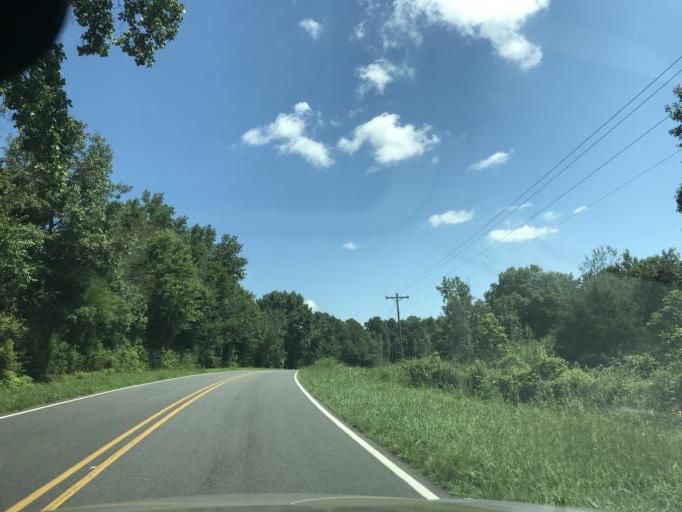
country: US
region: Georgia
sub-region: Dawson County
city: Dawsonville
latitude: 34.3312
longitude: -84.0486
